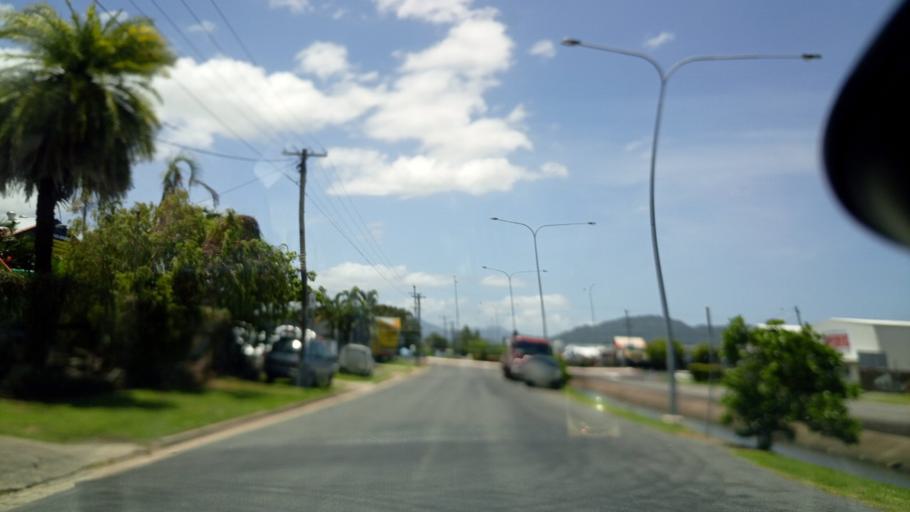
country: AU
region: Queensland
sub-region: Cairns
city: Woree
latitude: -16.9375
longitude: 145.7576
